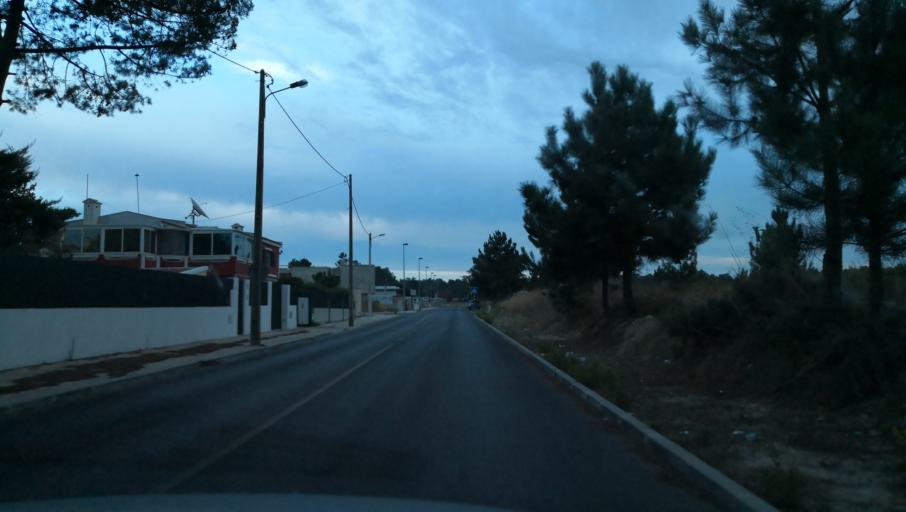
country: PT
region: Setubal
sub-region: Seixal
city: Amora
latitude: 38.5970
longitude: -9.1487
